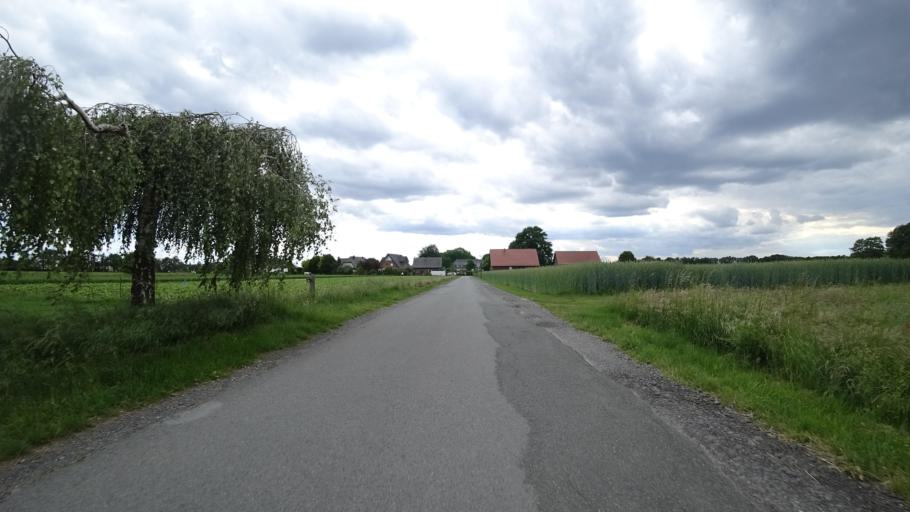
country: DE
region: North Rhine-Westphalia
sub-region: Regierungsbezirk Detmold
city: Guetersloh
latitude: 51.8967
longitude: 8.4414
